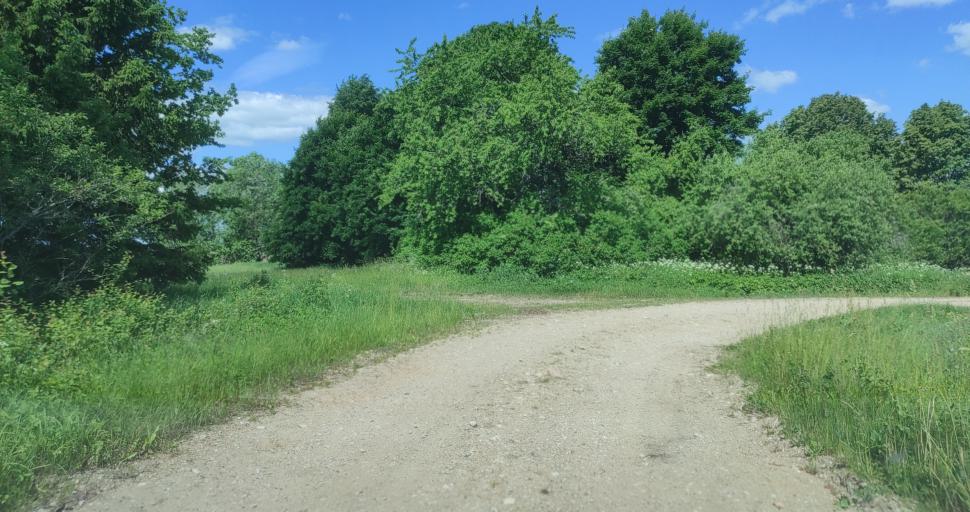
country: LV
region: Aizpute
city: Aizpute
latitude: 56.8587
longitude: 21.7069
